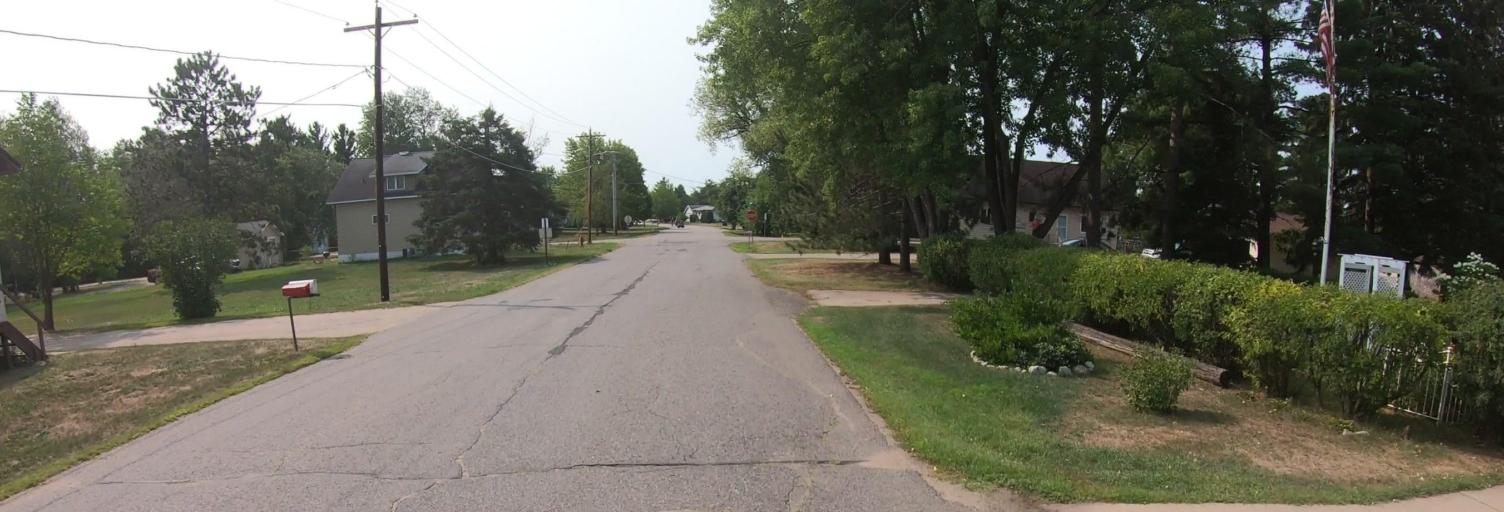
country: US
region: Minnesota
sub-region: Saint Louis County
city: Parkville
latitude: 47.5144
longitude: -92.5677
